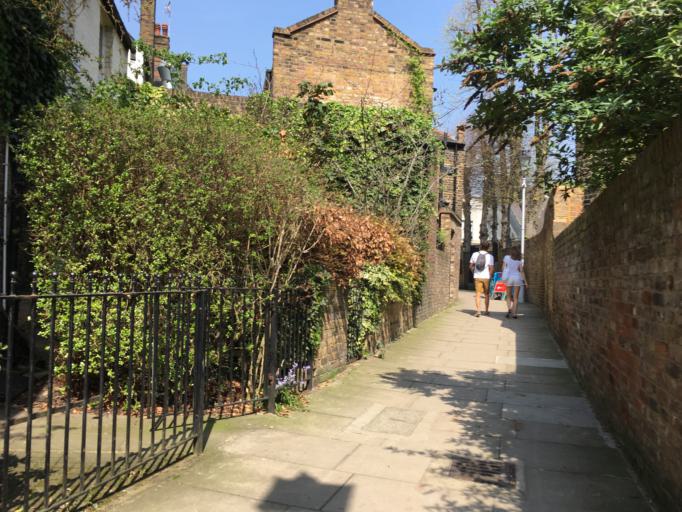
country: GB
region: England
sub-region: Greater London
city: Camden Town
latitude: 51.5545
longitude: -0.1441
